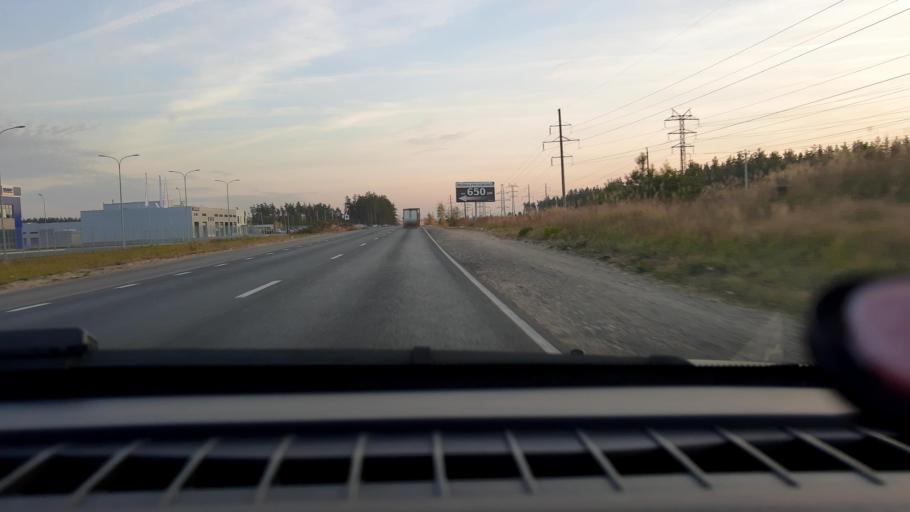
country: RU
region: Nizjnij Novgorod
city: Babino
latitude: 56.3086
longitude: 43.5591
